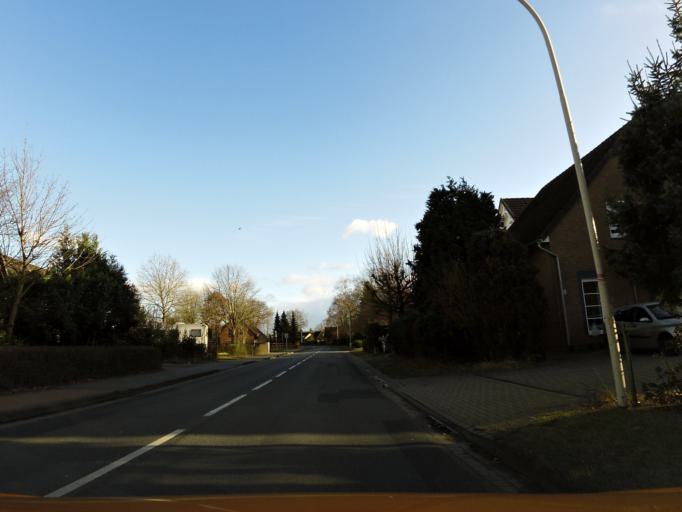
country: DE
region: Lower Saxony
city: Verden
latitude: 52.9077
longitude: 9.2642
